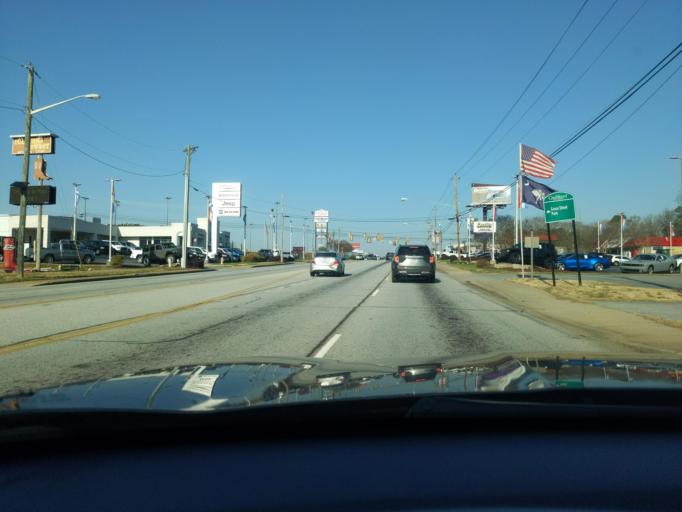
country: US
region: South Carolina
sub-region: Greenwood County
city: Greenwood
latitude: 34.2157
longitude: -82.1559
